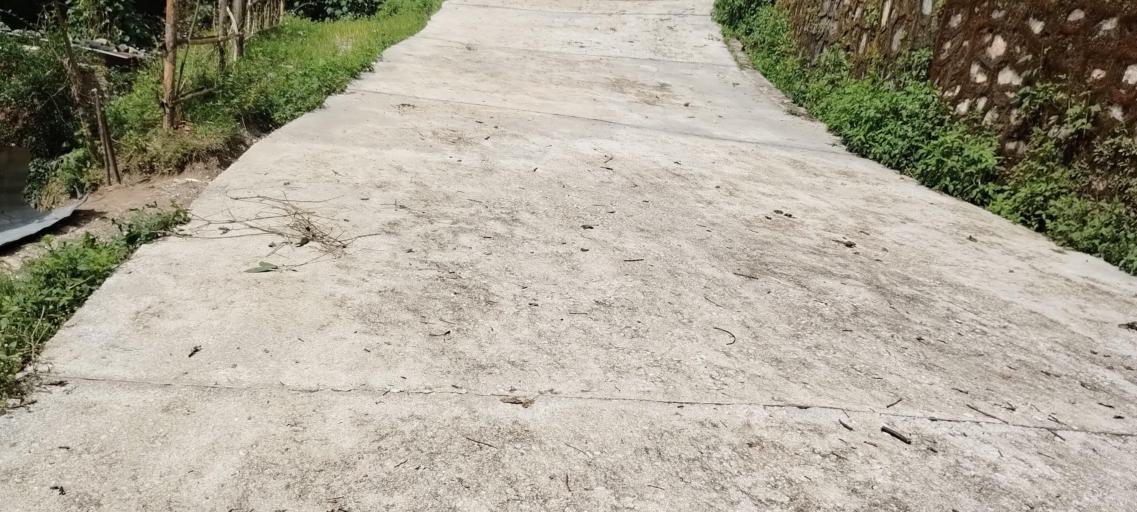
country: NP
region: Central Region
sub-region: Bagmati Zone
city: Kathmandu
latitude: 27.7912
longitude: 85.3628
